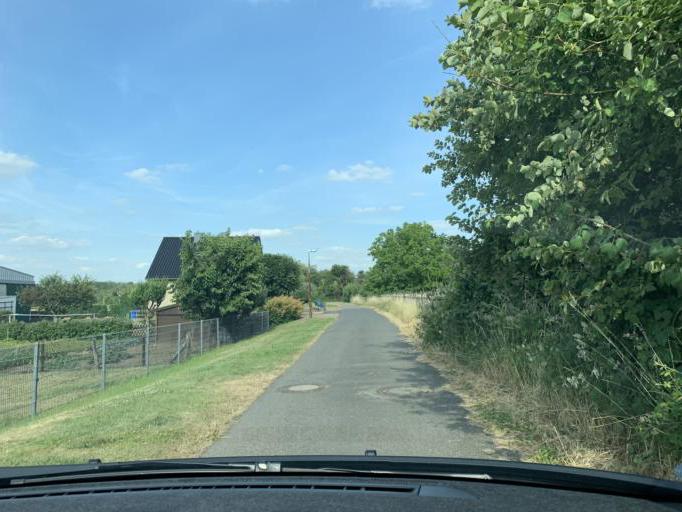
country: DE
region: North Rhine-Westphalia
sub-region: Regierungsbezirk Koln
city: Dueren
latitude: 50.8194
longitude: 6.4911
